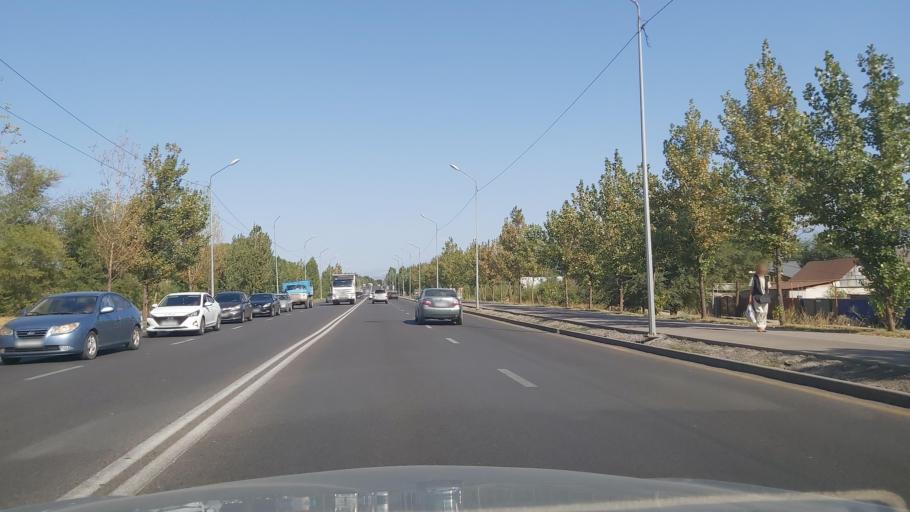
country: KZ
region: Almaty Oblysy
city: Burunday
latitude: 43.3125
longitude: 76.8556
